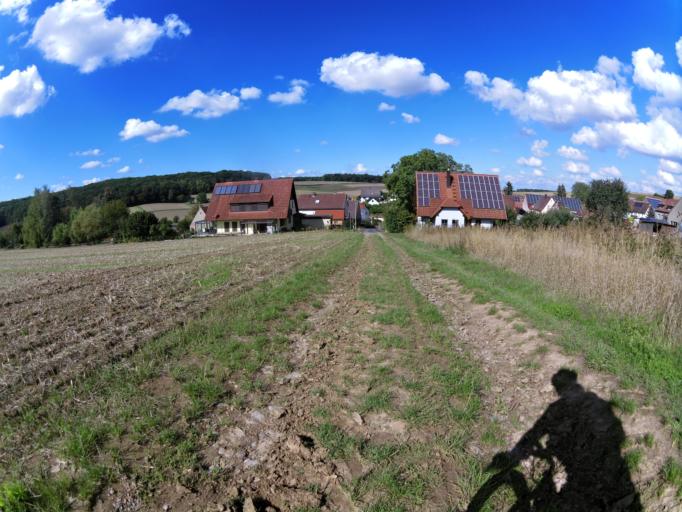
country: DE
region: Bavaria
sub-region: Regierungsbezirk Unterfranken
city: Frickenhausen
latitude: 49.6884
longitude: 10.0867
